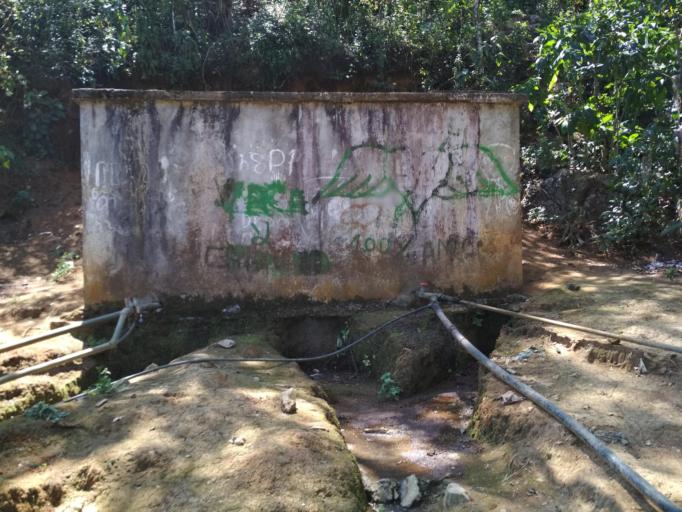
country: MX
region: Veracruz
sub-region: Tlilapan
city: Tonalixco
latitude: 18.7754
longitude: -97.0755
